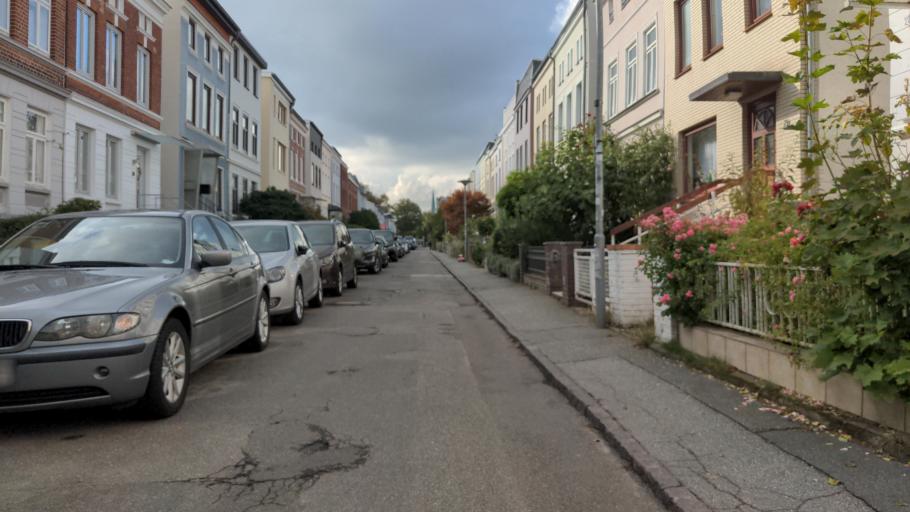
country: DE
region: Schleswig-Holstein
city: Luebeck
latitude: 53.8662
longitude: 10.7030
